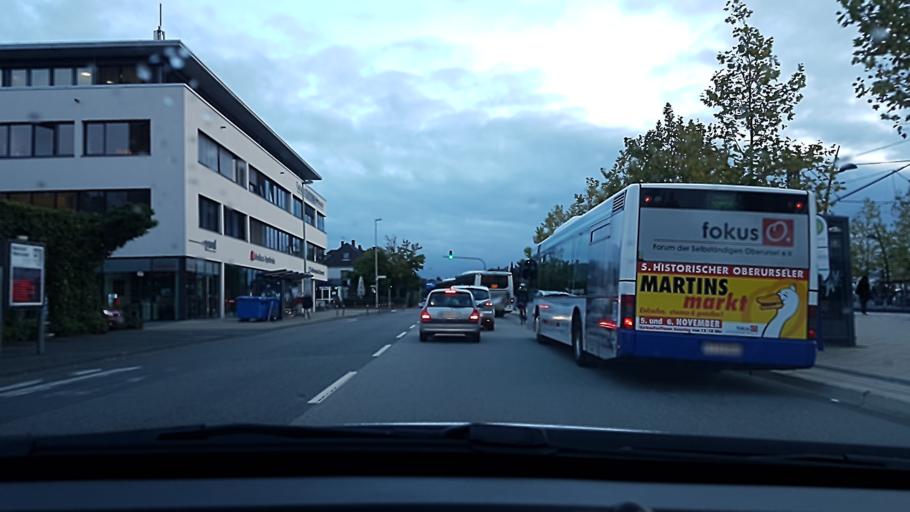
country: DE
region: Hesse
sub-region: Regierungsbezirk Darmstadt
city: Oberursel
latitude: 50.1989
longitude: 8.5867
